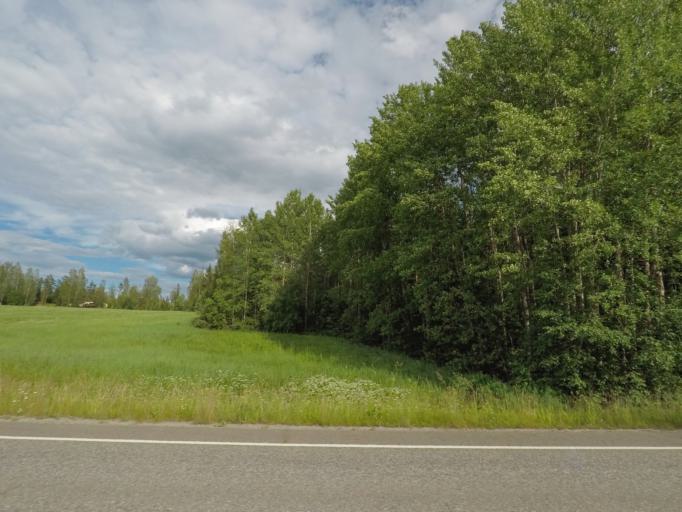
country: FI
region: Paijanne Tavastia
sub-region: Lahti
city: Hollola
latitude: 60.8189
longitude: 25.4846
